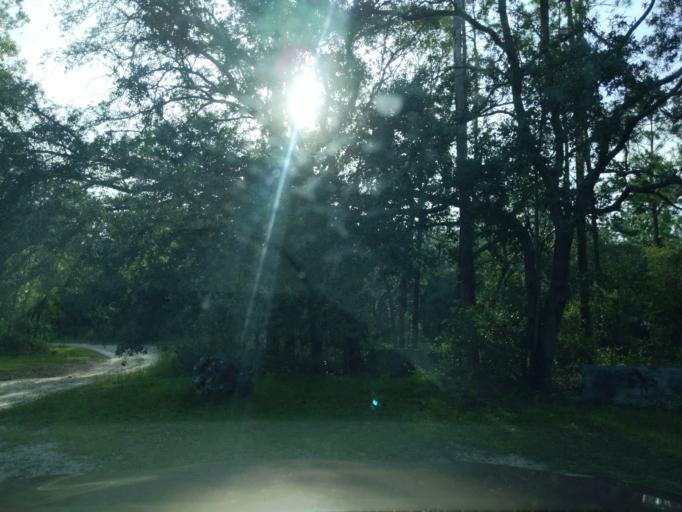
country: US
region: Florida
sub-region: Gadsden County
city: Midway
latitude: 30.3768
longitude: -84.3982
